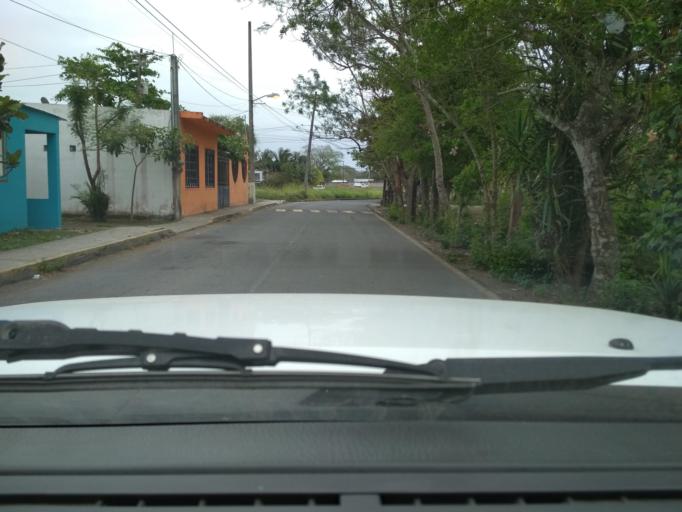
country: MX
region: Veracruz
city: Paso del Toro
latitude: 19.0552
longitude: -96.1344
